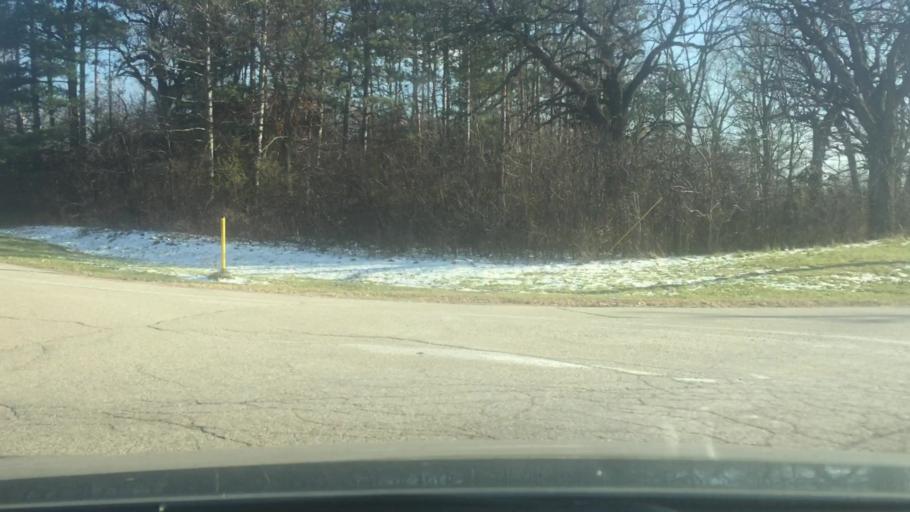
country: US
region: Wisconsin
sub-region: Jefferson County
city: Palmyra
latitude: 42.9175
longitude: -88.5420
